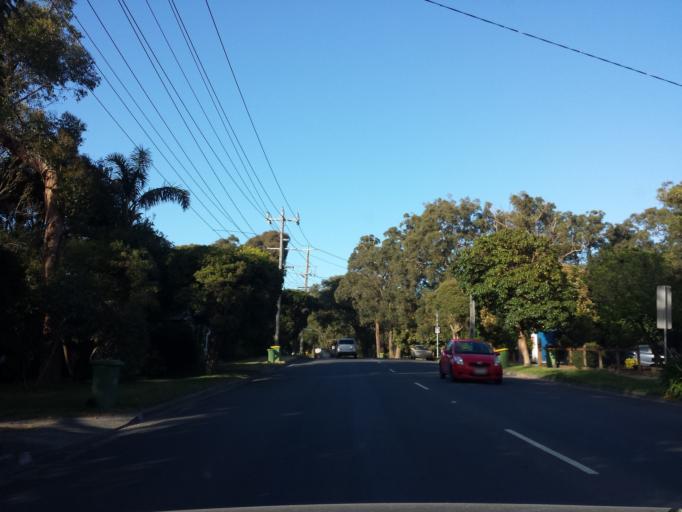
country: AU
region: Victoria
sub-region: Yarra Ranges
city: Belgrave Heights
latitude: -37.9321
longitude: 145.3582
